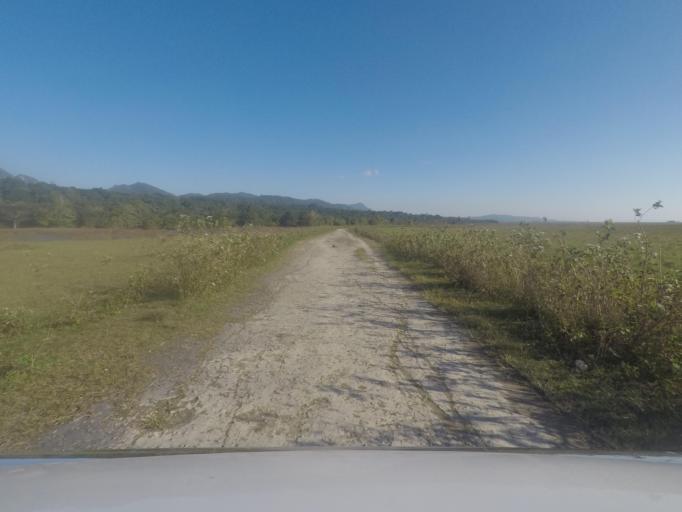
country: TL
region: Lautem
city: Lospalos
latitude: -8.4149
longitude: 127.1973
